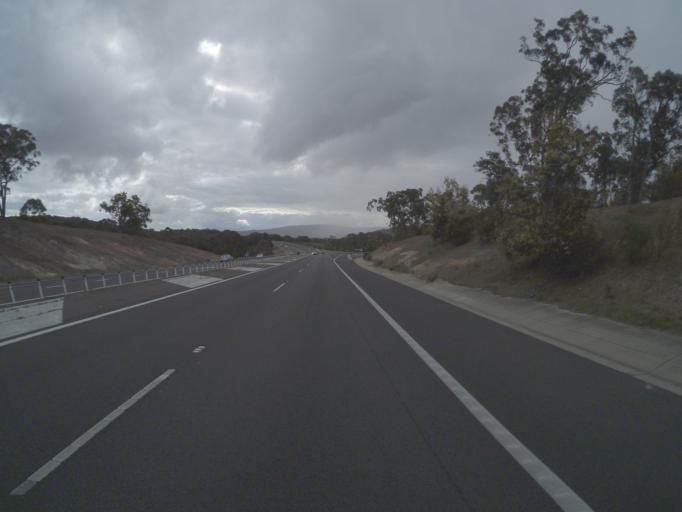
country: AU
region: New South Wales
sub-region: Goulburn Mulwaree
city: Goulburn
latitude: -34.7365
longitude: 149.8327
